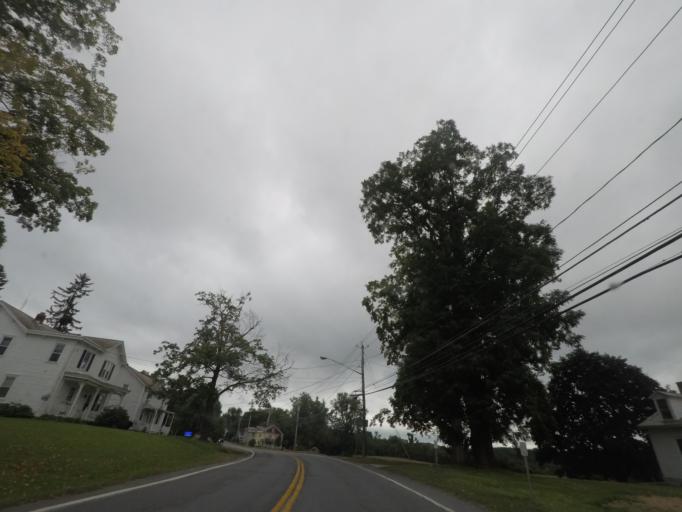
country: US
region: New York
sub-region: Rensselaer County
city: Hoosick Falls
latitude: 42.9254
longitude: -73.3471
